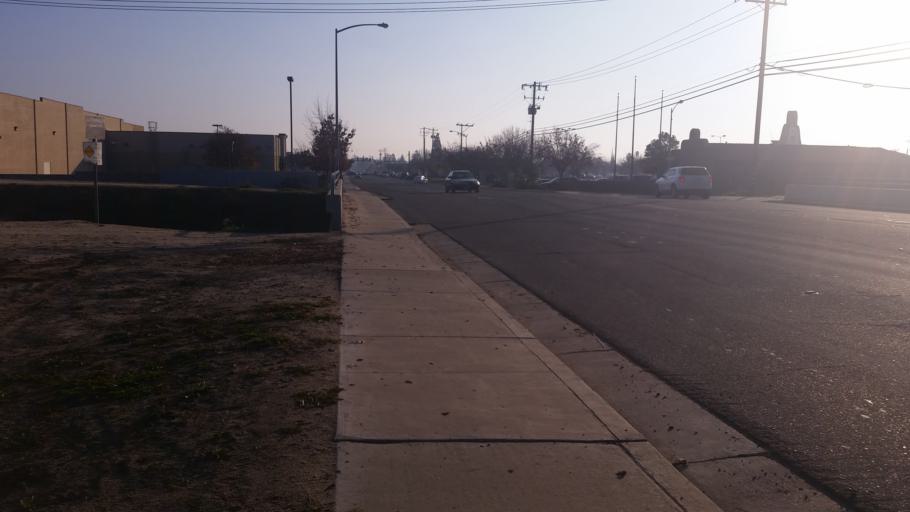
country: US
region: California
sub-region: Merced County
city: Atwater
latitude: 37.3632
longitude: -120.5956
